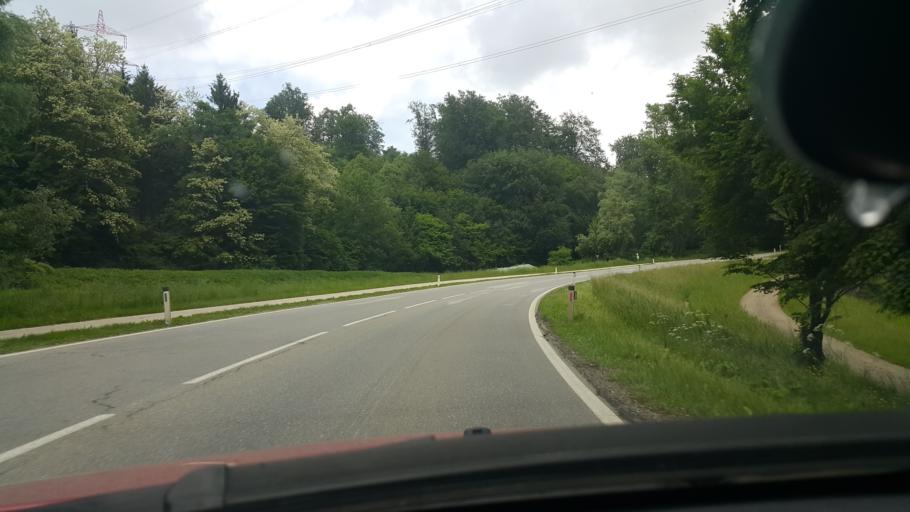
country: AT
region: Styria
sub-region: Politischer Bezirk Leibnitz
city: Weitendorf
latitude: 46.8718
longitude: 15.4779
